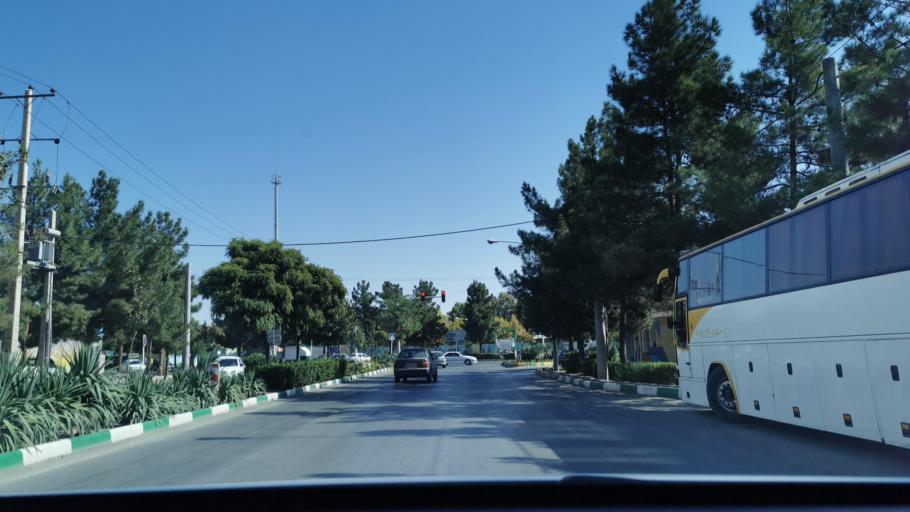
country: IR
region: Razavi Khorasan
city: Mashhad
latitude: 36.3355
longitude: 59.5933
